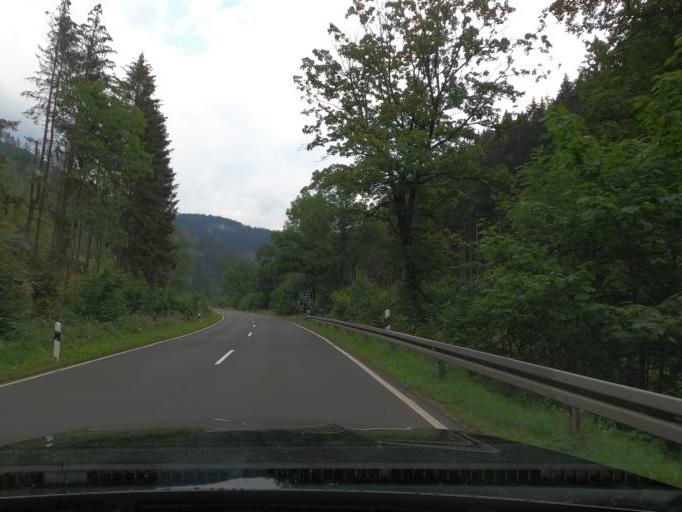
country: DE
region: Lower Saxony
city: Goslar
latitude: 51.8839
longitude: 10.3993
